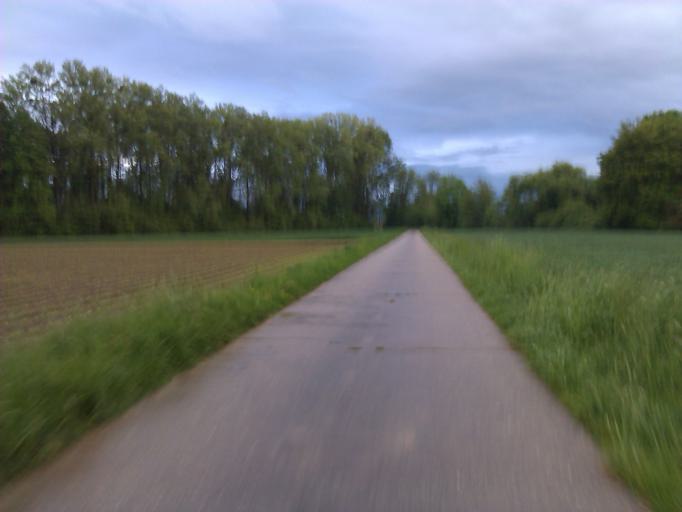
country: DE
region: Baden-Wuerttemberg
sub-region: Karlsruhe Region
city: Lichtenau
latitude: 48.6996
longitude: 7.9690
